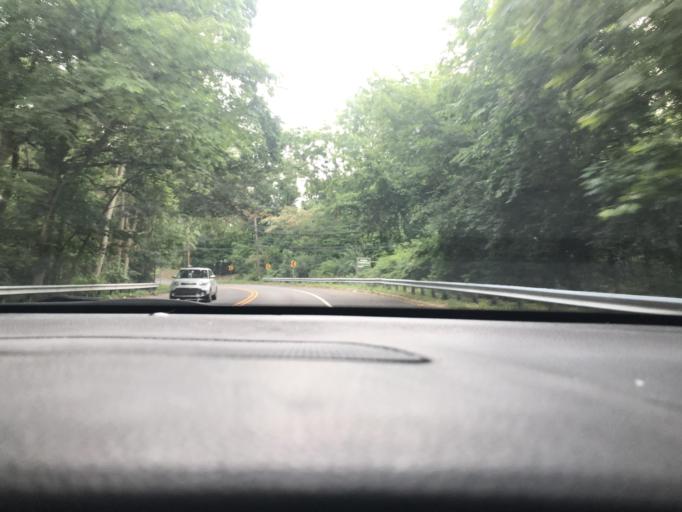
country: US
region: Pennsylvania
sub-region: Montgomery County
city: Blue Bell
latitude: 40.1689
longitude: -75.2516
